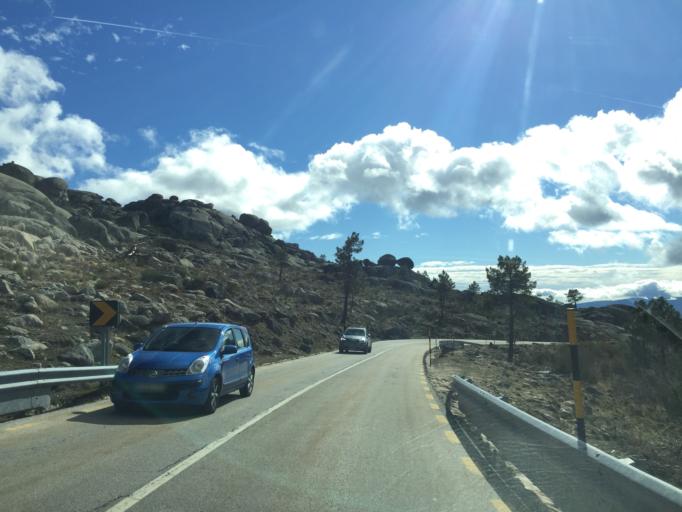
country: PT
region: Castelo Branco
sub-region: Covilha
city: Covilha
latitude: 40.3081
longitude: -7.5372
